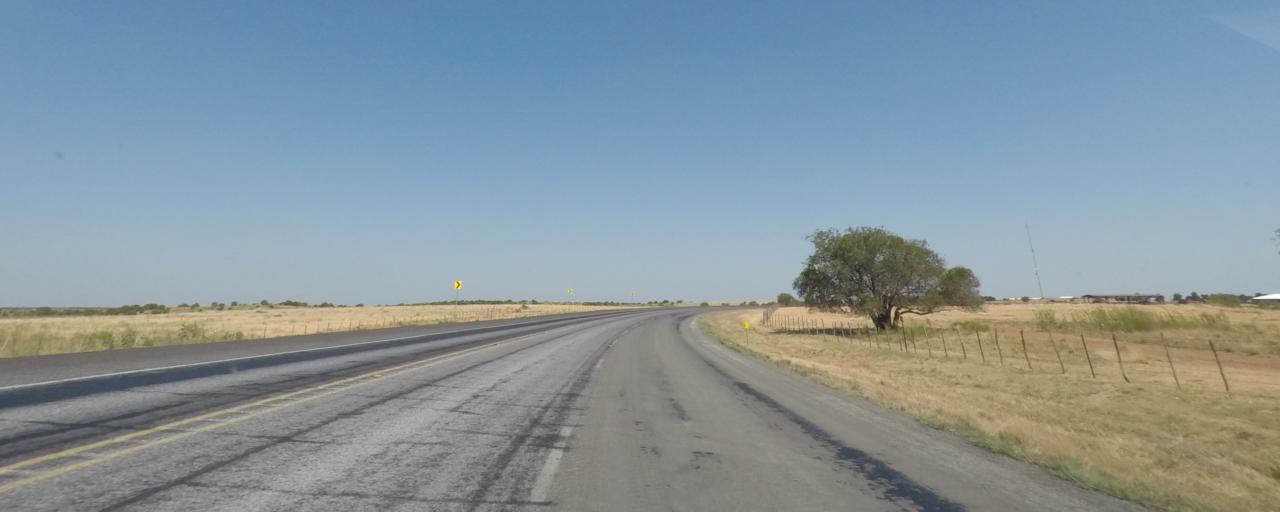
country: US
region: Texas
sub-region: King County
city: Guthrie
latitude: 33.6337
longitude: -100.3439
